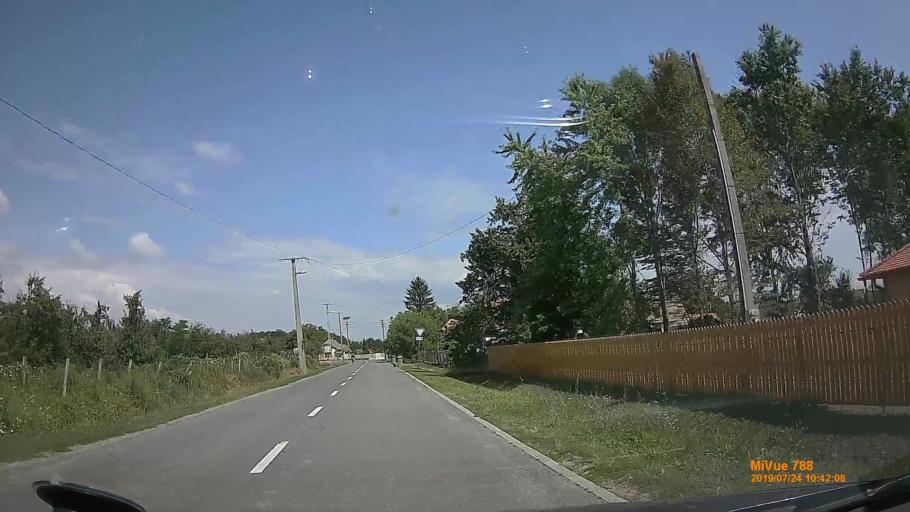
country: HU
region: Szabolcs-Szatmar-Bereg
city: Tarpa
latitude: 48.1959
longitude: 22.5472
